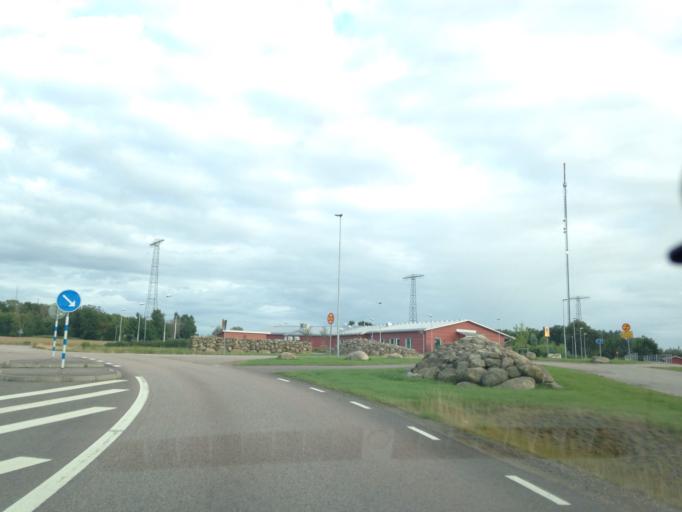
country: SE
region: Halland
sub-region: Varbergs Kommun
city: Tvaaker
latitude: 57.1163
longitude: 12.3916
